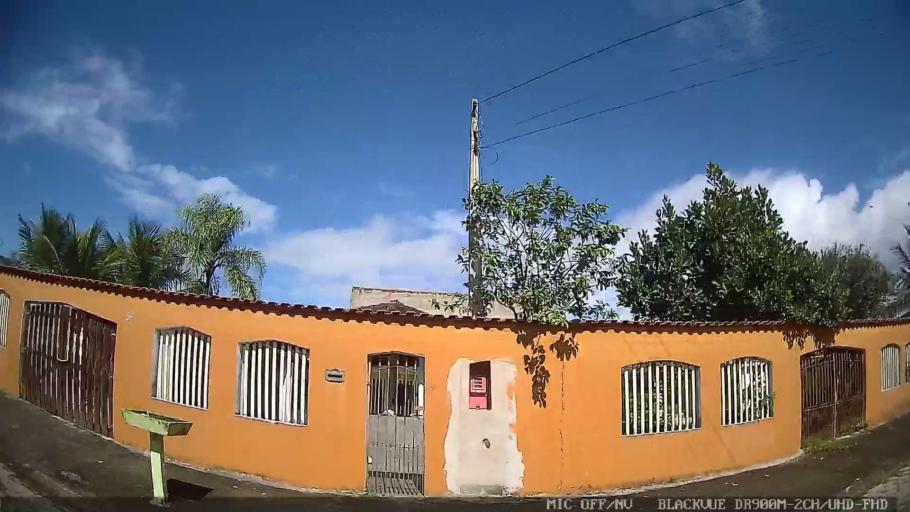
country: BR
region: Sao Paulo
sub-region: Itanhaem
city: Itanhaem
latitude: -24.2367
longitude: -46.8813
